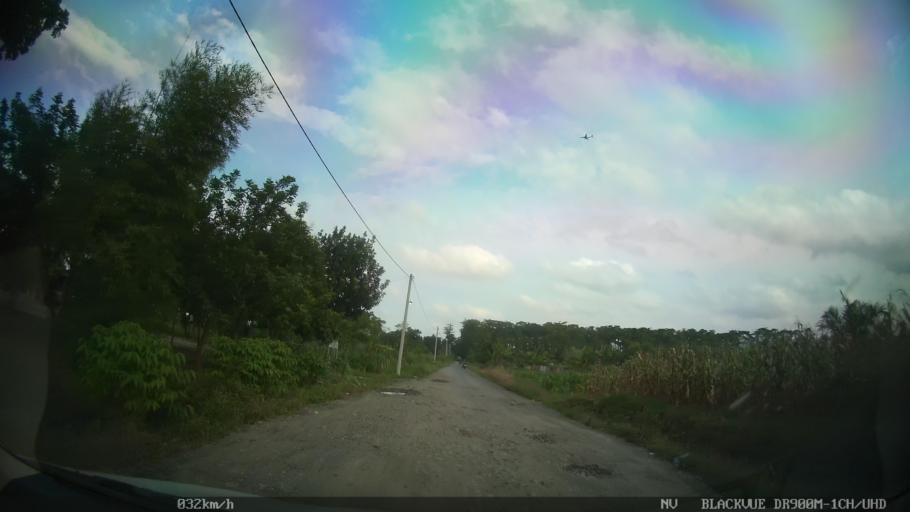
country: ID
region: North Sumatra
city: Percut
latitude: 3.5662
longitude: 98.7878
